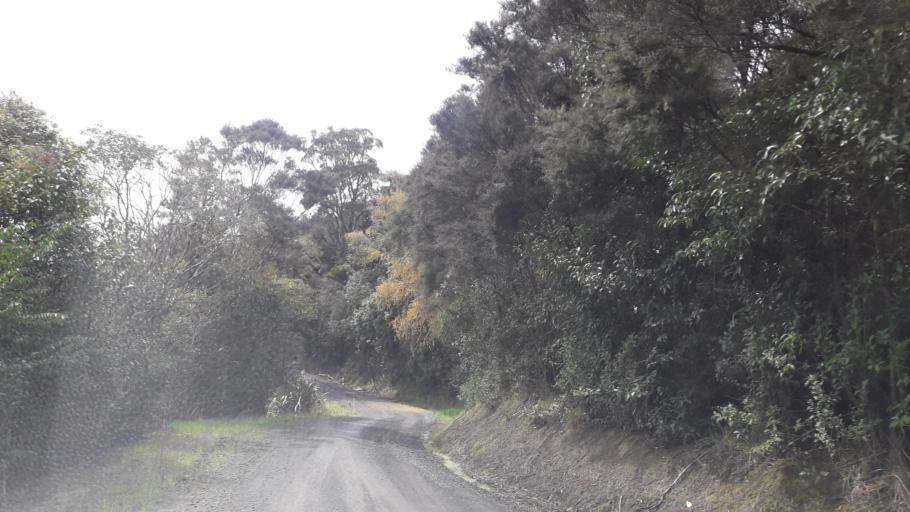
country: NZ
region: Northland
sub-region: Far North District
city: Waimate North
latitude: -35.3087
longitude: 173.5637
